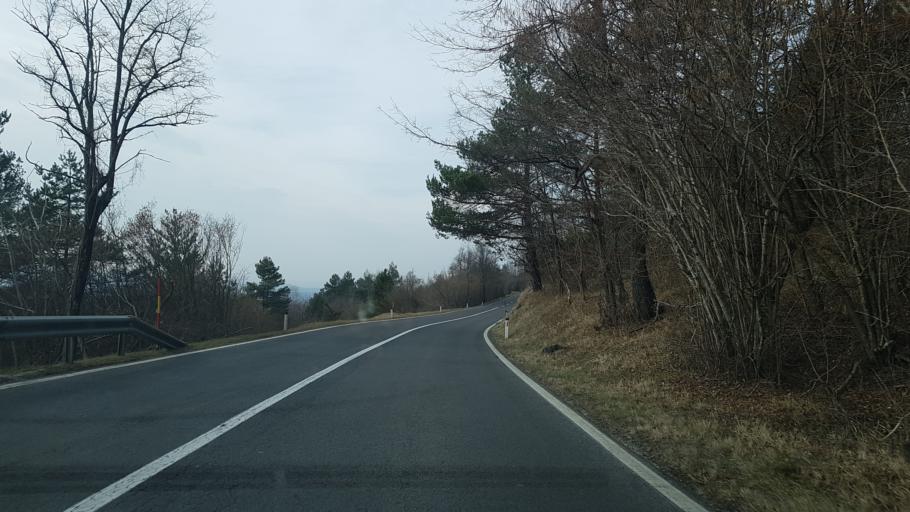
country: SI
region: Ilirska Bistrica
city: Ilirska Bistrica
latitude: 45.5012
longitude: 14.1808
